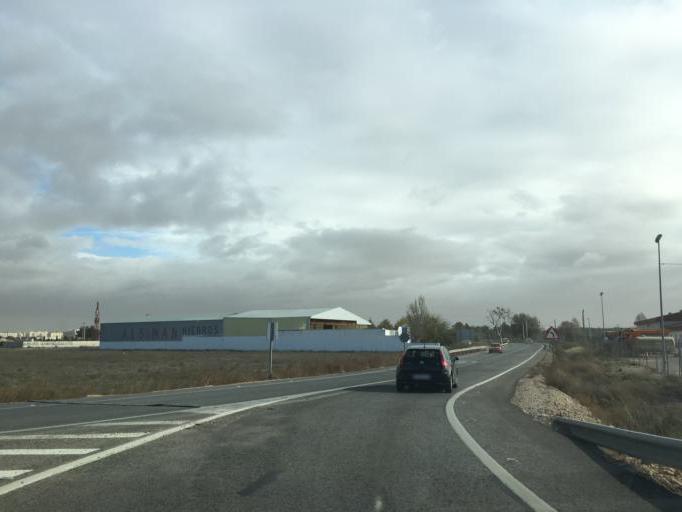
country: ES
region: Castille-La Mancha
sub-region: Provincia de Albacete
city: Albacete
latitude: 38.9981
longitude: -1.8949
